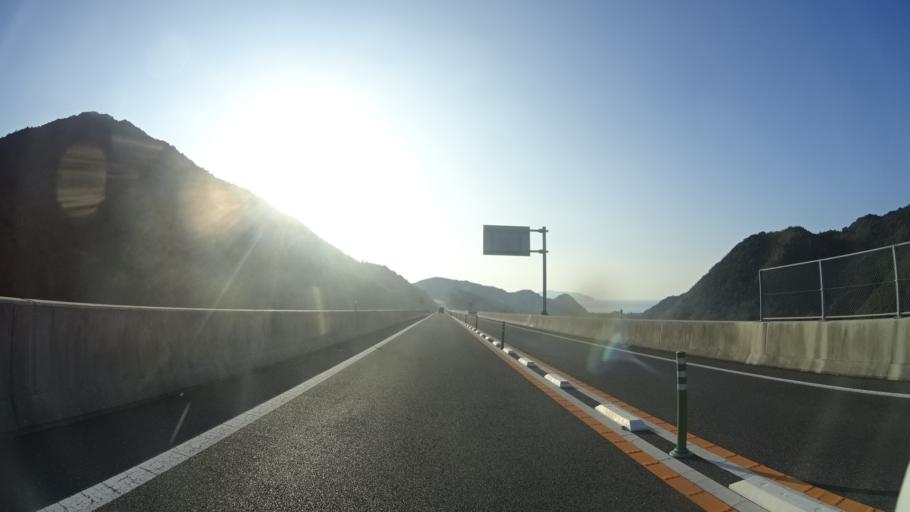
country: JP
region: Yamaguchi
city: Hagi
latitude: 34.3868
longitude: 131.3431
